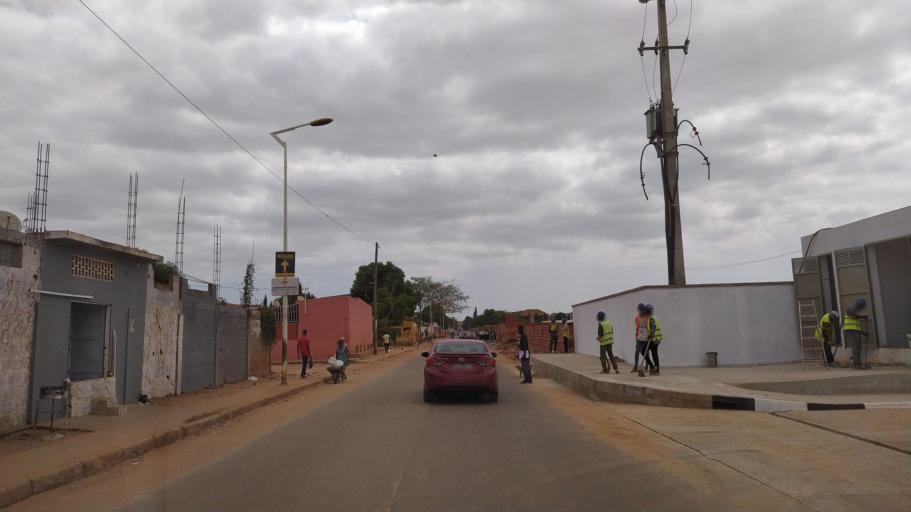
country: AO
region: Luanda
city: Luanda
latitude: -8.9316
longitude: 13.2589
